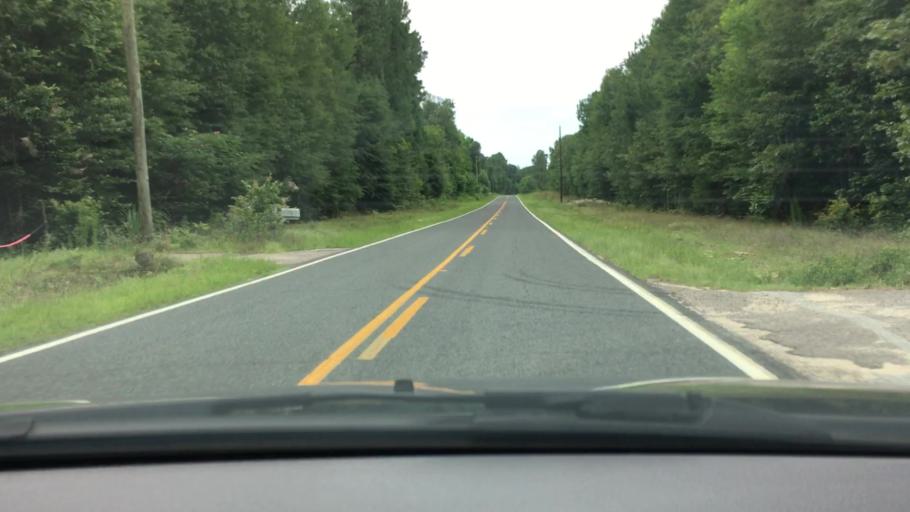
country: US
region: South Carolina
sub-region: Barnwell County
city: Williston
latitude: 33.6354
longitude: -81.3640
